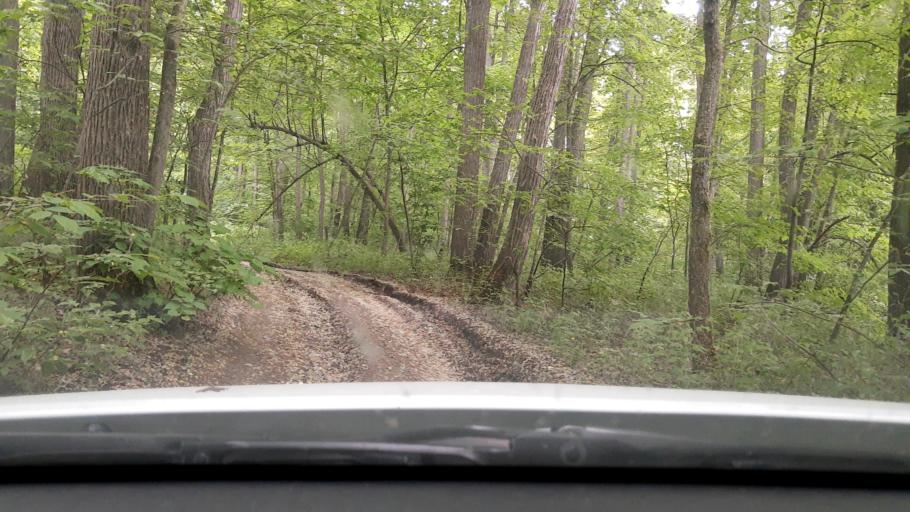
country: RU
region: Bashkortostan
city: Ufa
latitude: 54.6593
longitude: 55.8754
